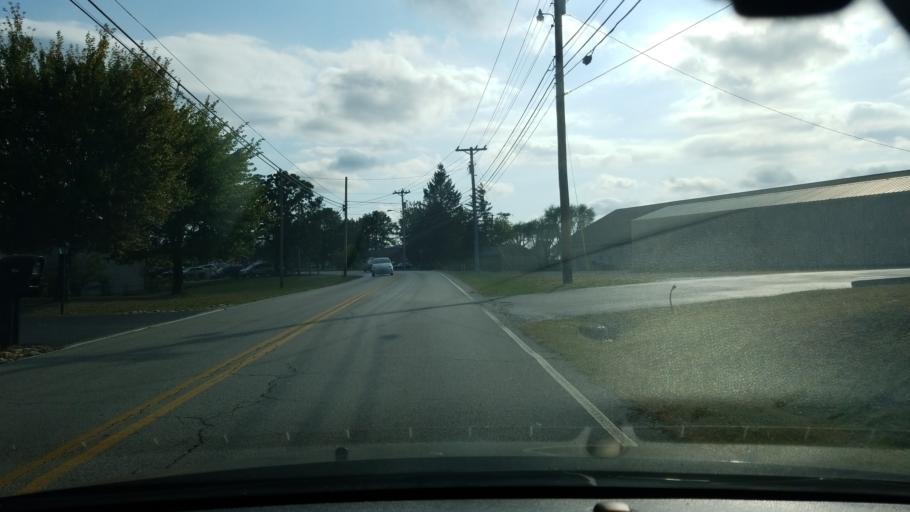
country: US
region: Tennessee
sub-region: Cumberland County
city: Crossville
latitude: 35.9720
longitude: -85.0363
